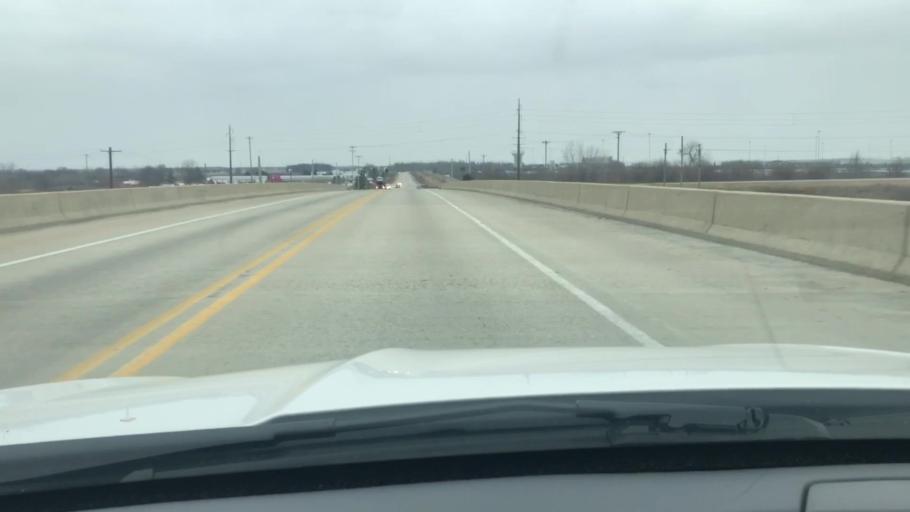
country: US
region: Indiana
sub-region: Tippecanoe County
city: Dayton
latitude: 40.3742
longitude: -86.8141
